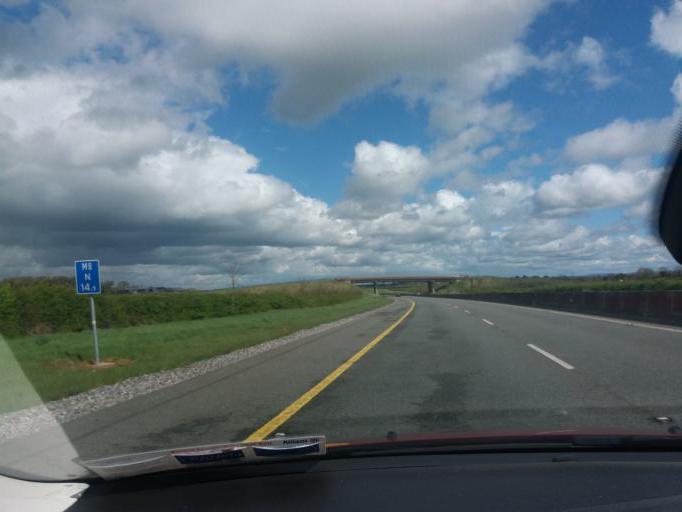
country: IE
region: Leinster
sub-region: Laois
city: Rathdowney
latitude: 52.8057
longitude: -7.4991
